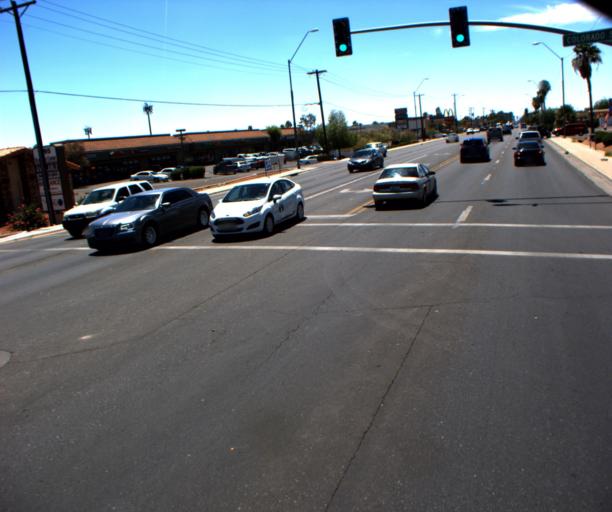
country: US
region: Arizona
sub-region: Pinal County
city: Casa Grande
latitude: 32.8796
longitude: -111.7313
